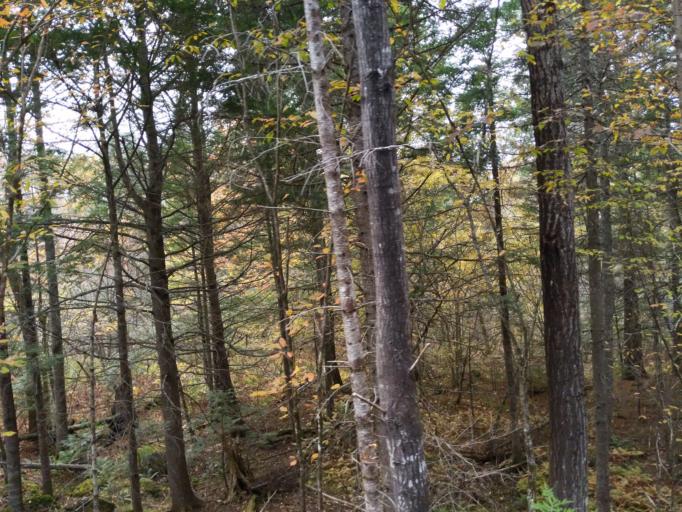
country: US
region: Maine
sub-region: Lincoln County
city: Whitefield
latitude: 44.1008
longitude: -69.6201
